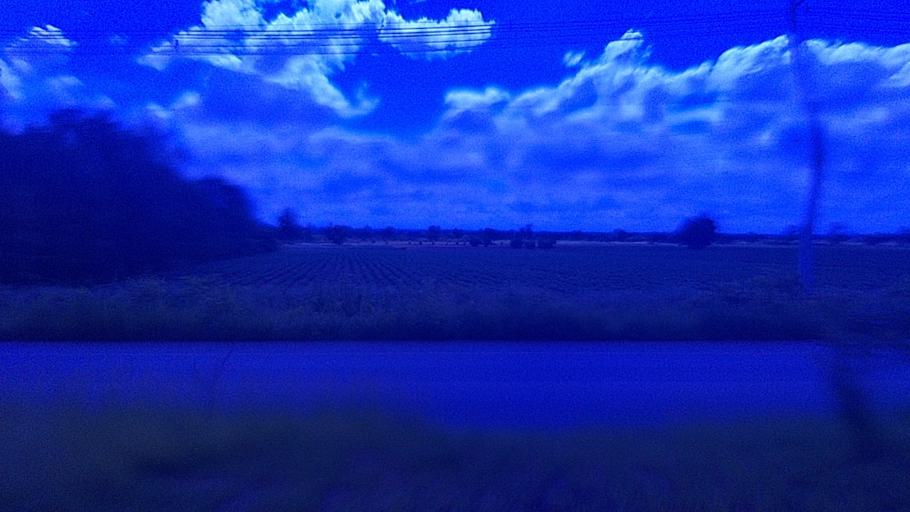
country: TH
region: Nakhon Ratchasima
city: Dan Khun Thot
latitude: 15.0914
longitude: 101.7194
